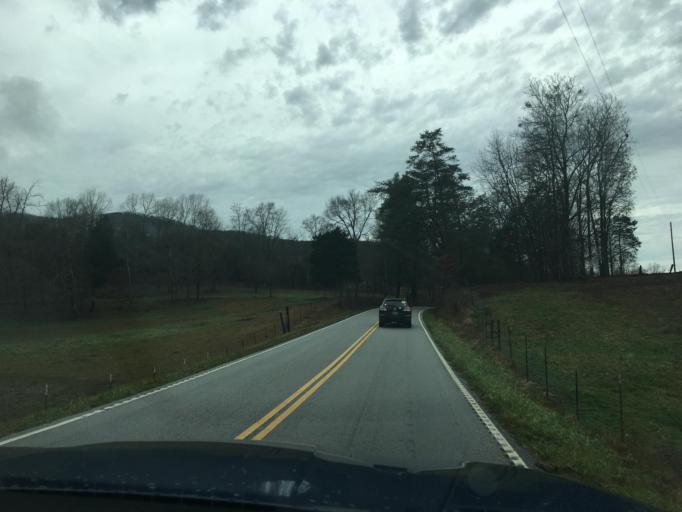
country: US
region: Tennessee
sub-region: McMinn County
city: Englewood
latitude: 35.3420
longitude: -84.3870
